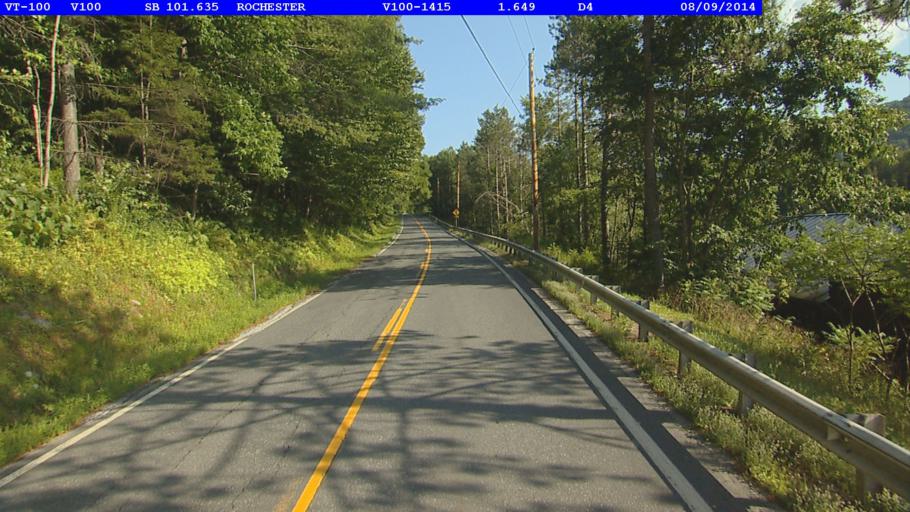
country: US
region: Vermont
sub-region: Orange County
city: Randolph
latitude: 43.8265
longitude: -72.7915
